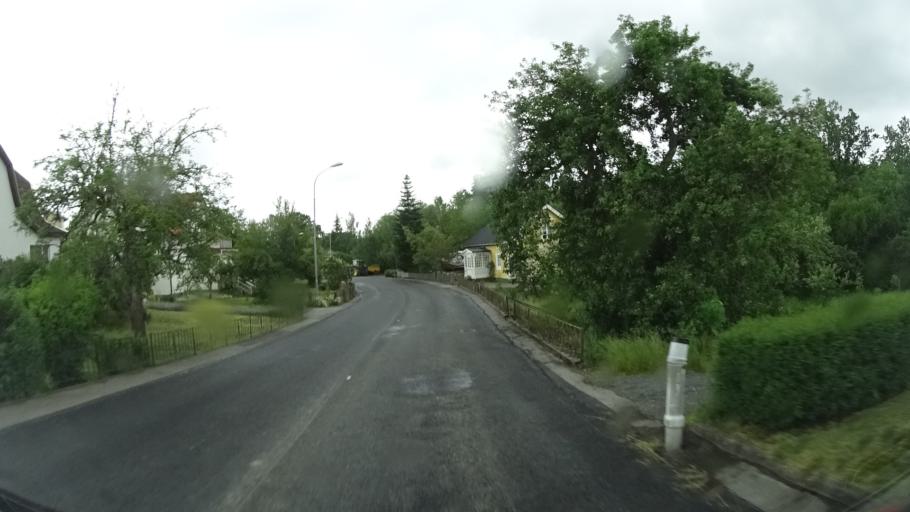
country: SE
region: Kalmar
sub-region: Oskarshamns Kommun
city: Oskarshamn
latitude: 57.3990
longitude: 16.1967
